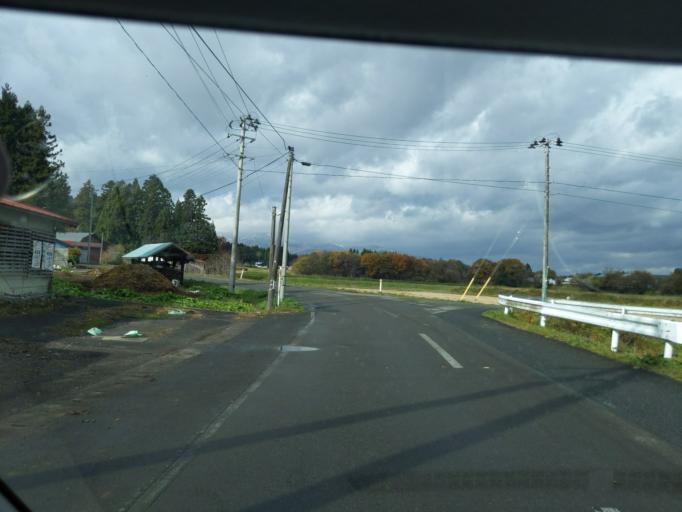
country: JP
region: Iwate
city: Mizusawa
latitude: 39.0906
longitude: 141.0173
